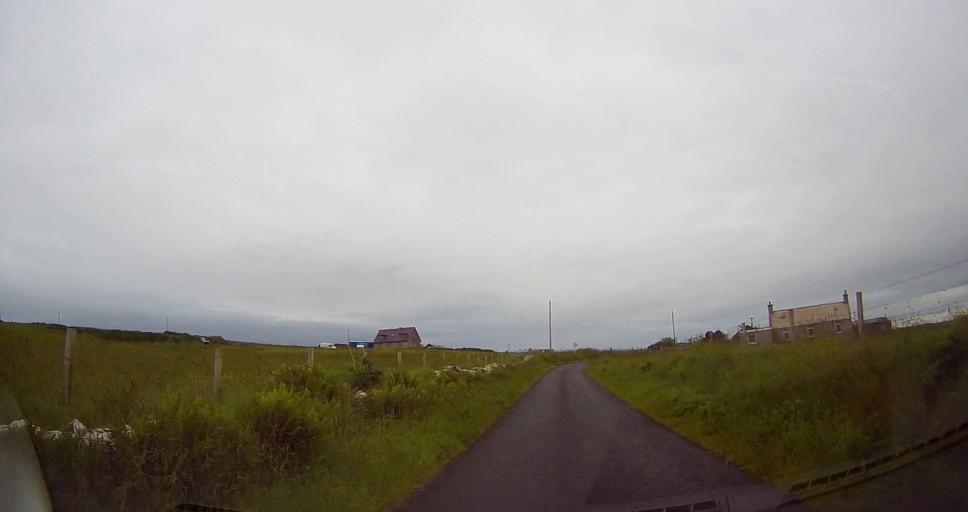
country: GB
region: Scotland
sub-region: Orkney Islands
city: Stromness
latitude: 59.1256
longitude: -3.2828
